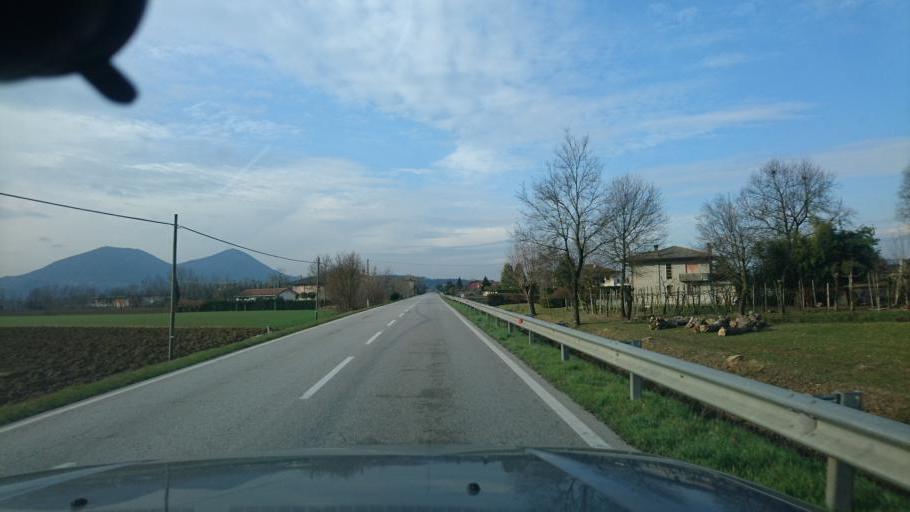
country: IT
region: Veneto
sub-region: Provincia di Padova
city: Cervarese Santa Croce
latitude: 45.4069
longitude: 11.7017
